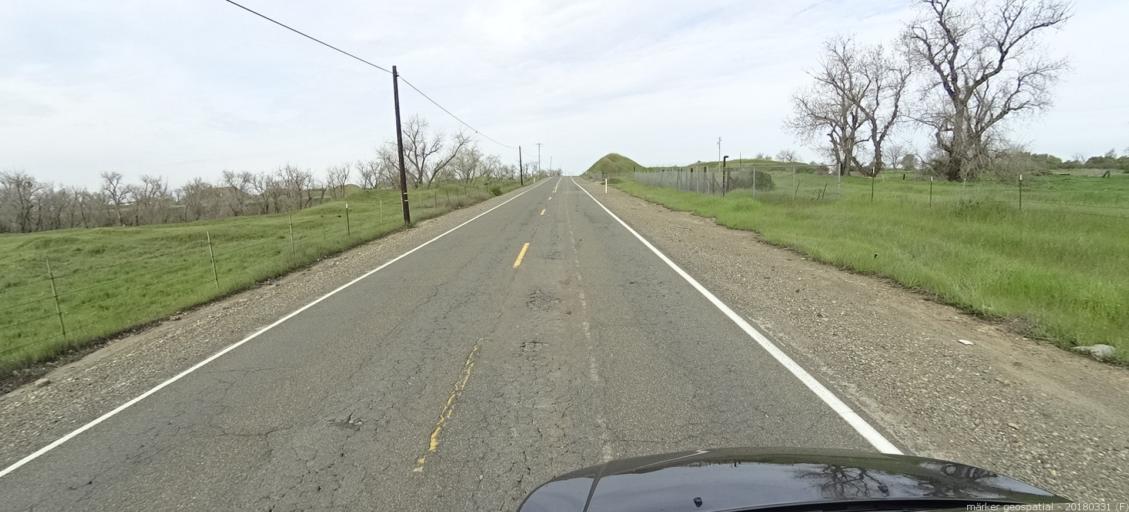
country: US
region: California
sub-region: Sacramento County
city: Gold River
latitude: 38.5939
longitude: -121.1928
